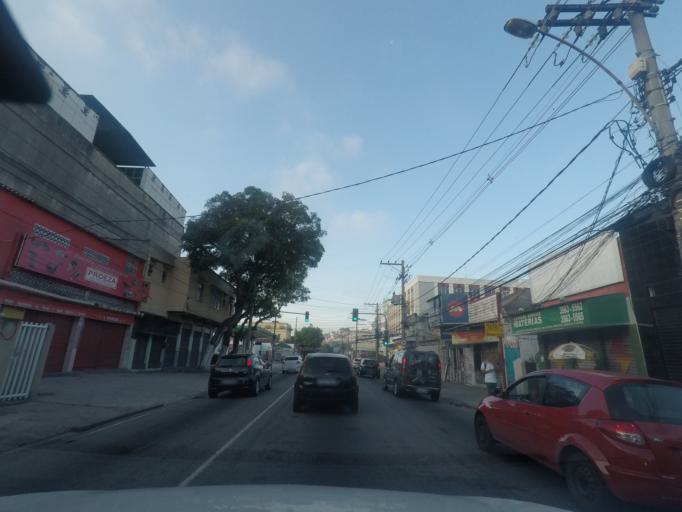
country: BR
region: Rio de Janeiro
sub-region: Duque De Caxias
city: Duque de Caxias
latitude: -22.8321
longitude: -43.2793
